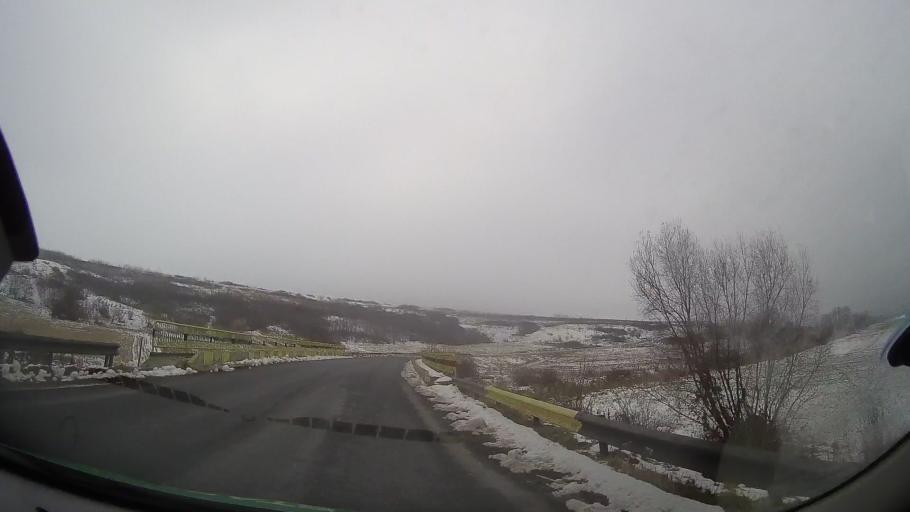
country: RO
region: Vaslui
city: Coroiesti
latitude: 46.2175
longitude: 27.4690
